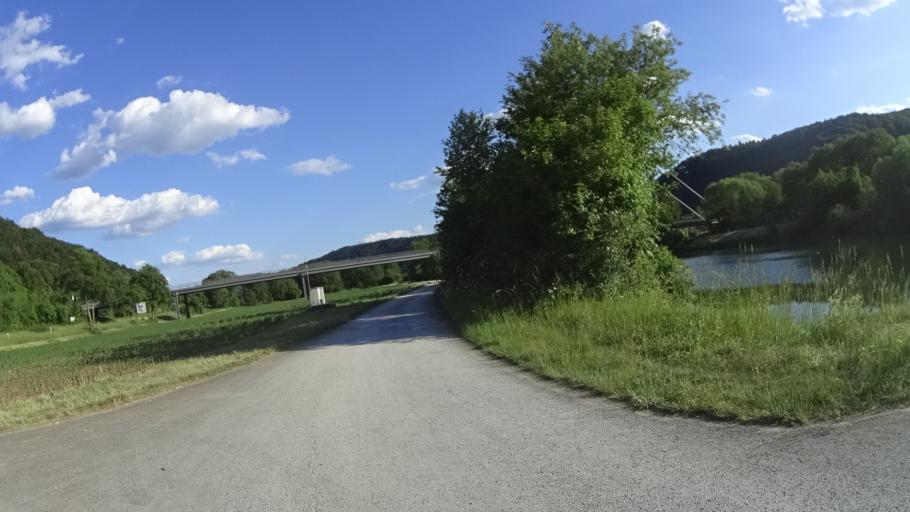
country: DE
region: Bavaria
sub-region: Upper Palatinate
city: Dietfurt
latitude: 48.9950
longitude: 11.6315
